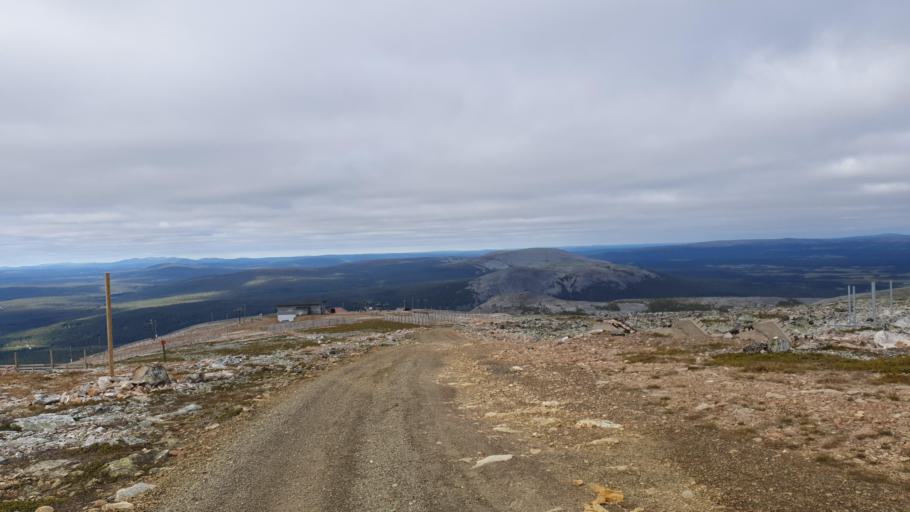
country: FI
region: Lapland
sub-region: Tunturi-Lappi
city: Kolari
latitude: 67.5677
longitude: 24.2094
